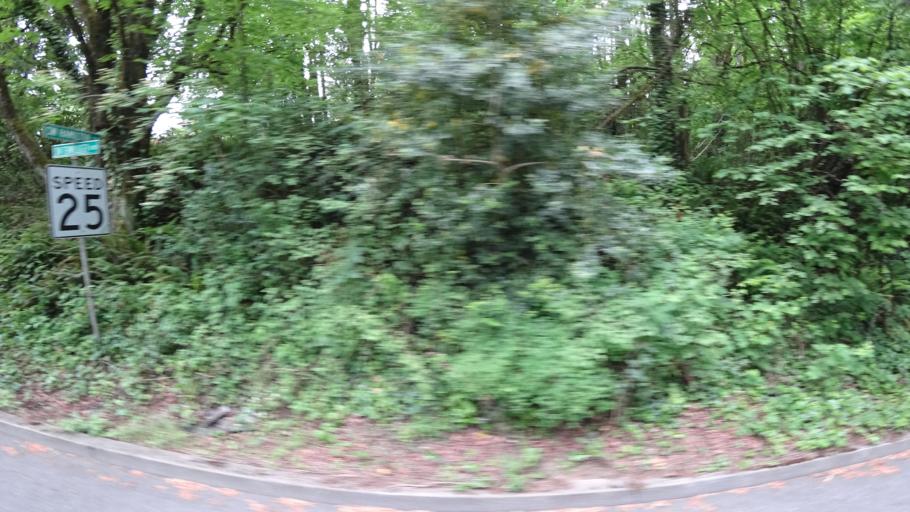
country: US
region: Oregon
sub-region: Multnomah County
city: Portland
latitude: 45.4933
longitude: -122.6814
